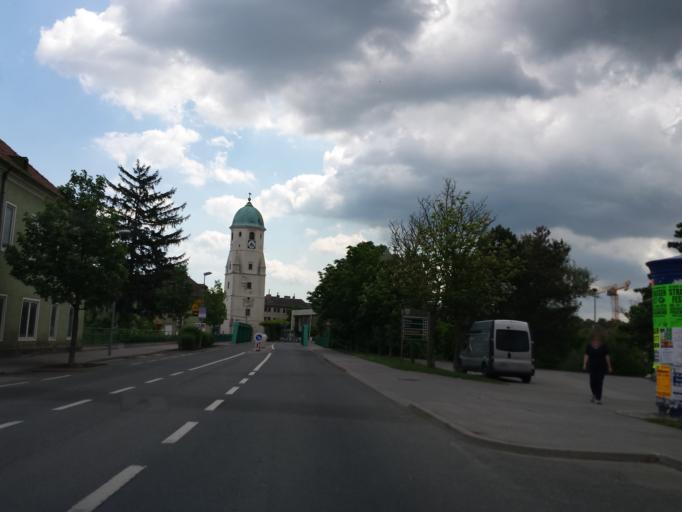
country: AT
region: Lower Austria
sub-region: Politischer Bezirk Wien-Umgebung
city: Fischamend Dorf
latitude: 48.1192
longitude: 16.6091
